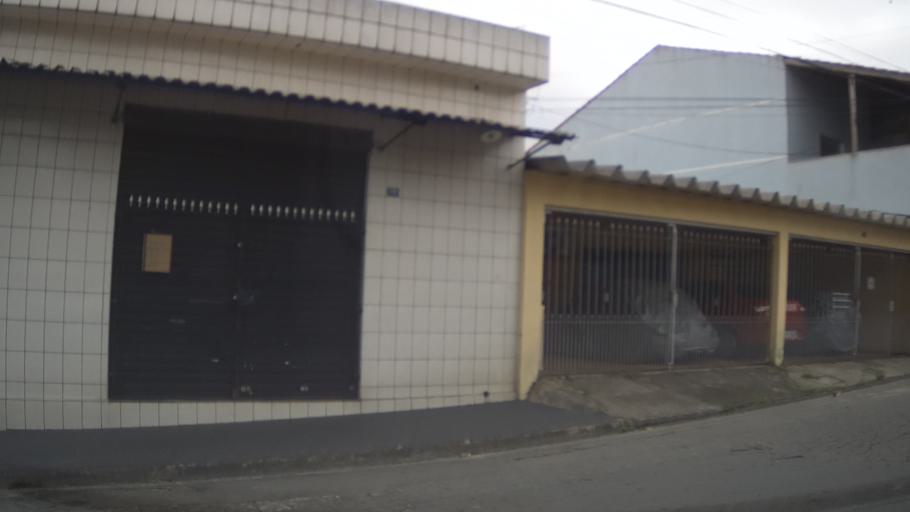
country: BR
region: Sao Paulo
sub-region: Guarulhos
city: Guarulhos
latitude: -23.4497
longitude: -46.5131
